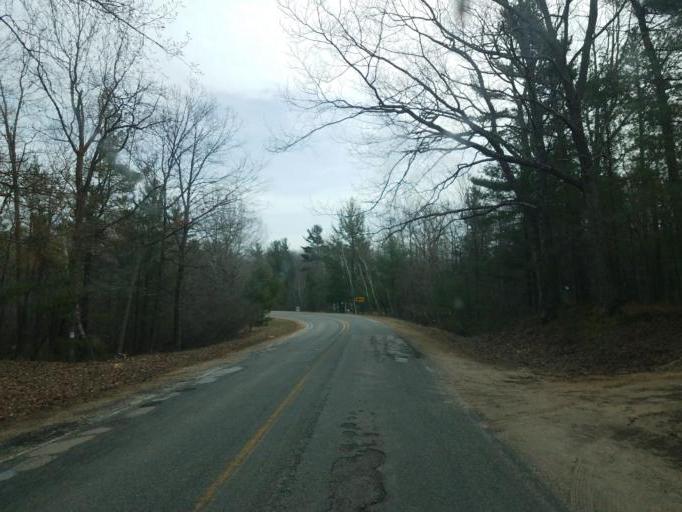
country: US
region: Michigan
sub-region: Oceana County
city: Hart
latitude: 43.7331
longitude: -86.4612
